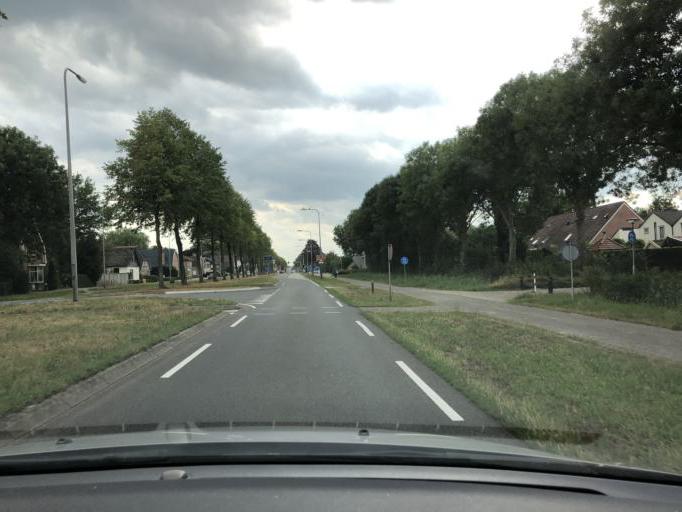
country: NL
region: Overijssel
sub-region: Gemeente Hardenberg
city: Hardenberg
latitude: 52.6271
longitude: 6.5616
